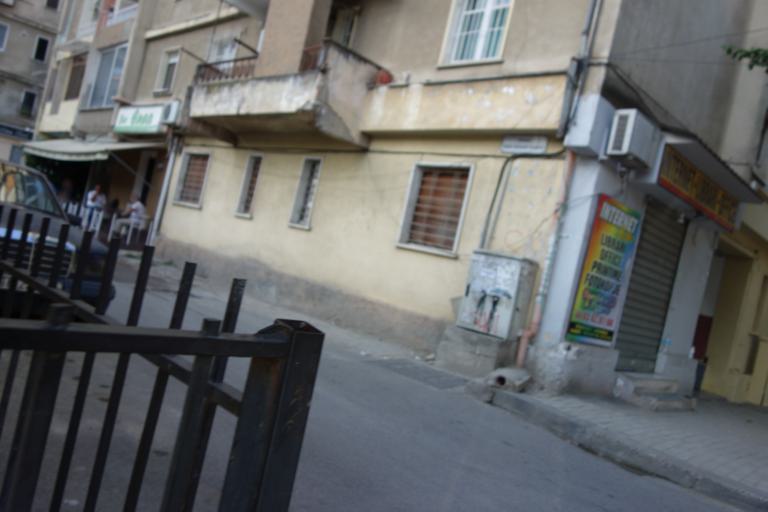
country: AL
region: Tirane
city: Tirana
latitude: 41.3327
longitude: 19.8161
